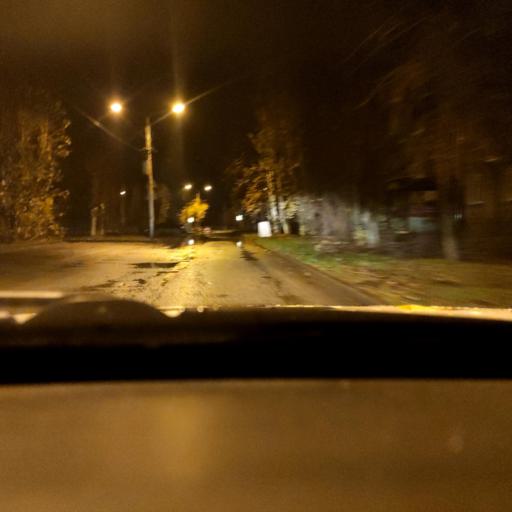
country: RU
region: Perm
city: Kultayevo
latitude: 58.0067
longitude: 55.9665
